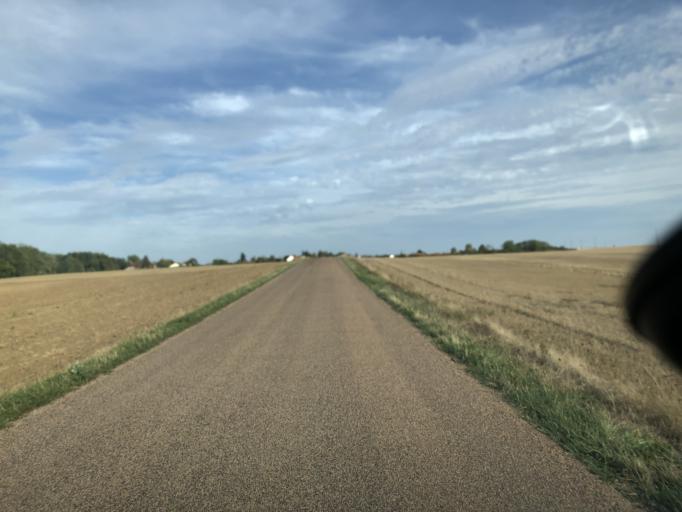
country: FR
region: Bourgogne
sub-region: Departement de l'Yonne
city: Joigny
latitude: 47.9594
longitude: 3.3904
